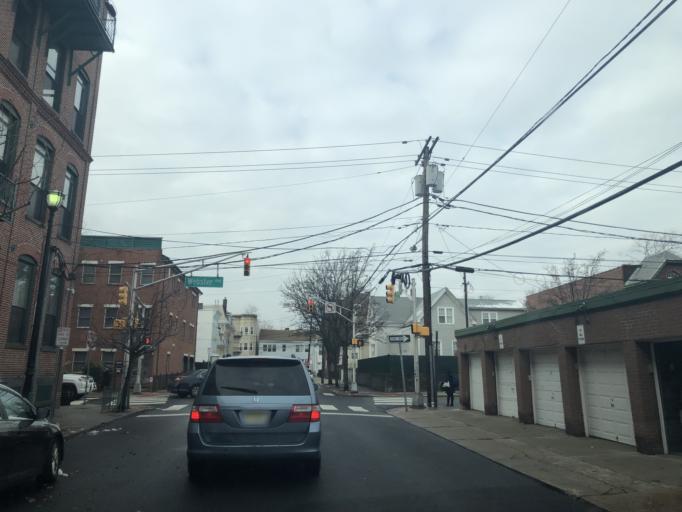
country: US
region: New Jersey
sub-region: Hudson County
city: Hoboken
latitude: 40.7429
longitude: -74.0465
